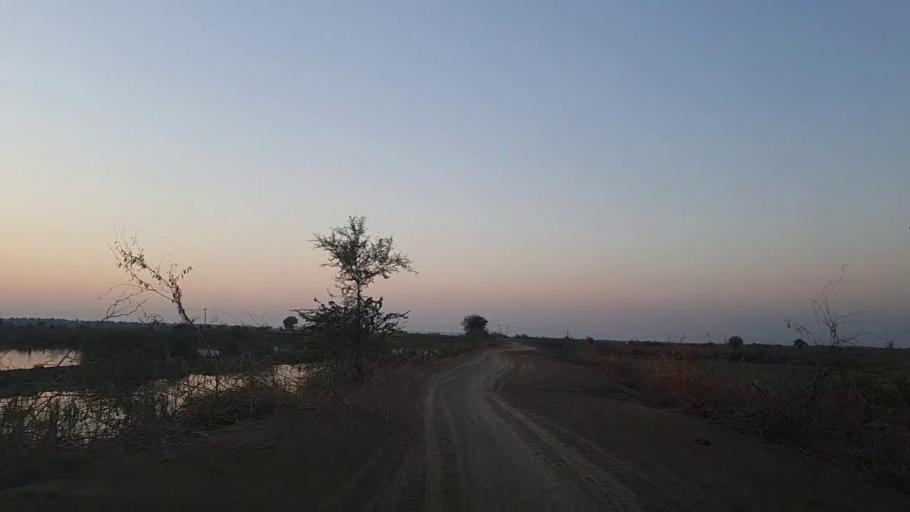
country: PK
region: Sindh
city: Tando Mittha Khan
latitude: 26.0659
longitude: 69.1610
